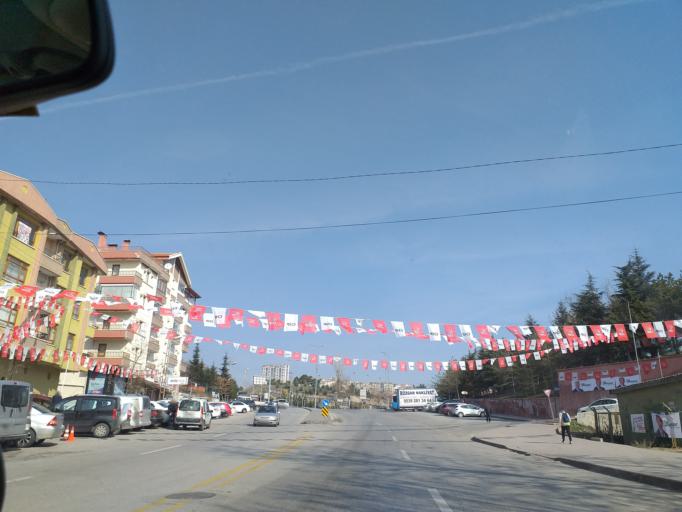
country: TR
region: Ankara
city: Ankara
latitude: 39.9980
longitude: 32.8547
